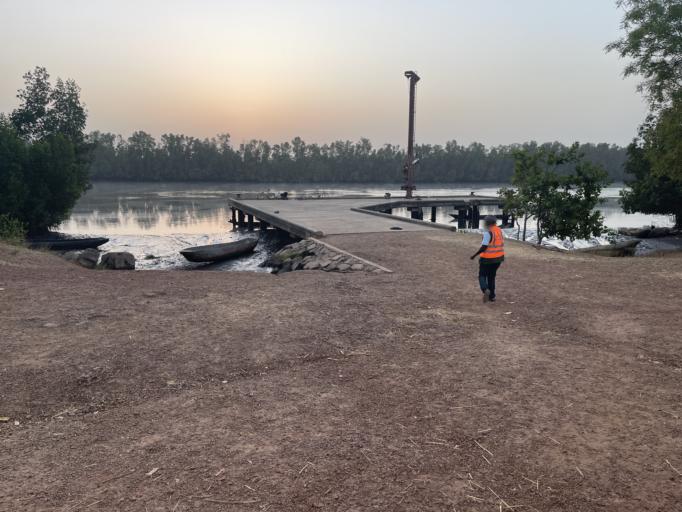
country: GW
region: Oio
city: Farim
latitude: 12.4198
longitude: -15.3149
